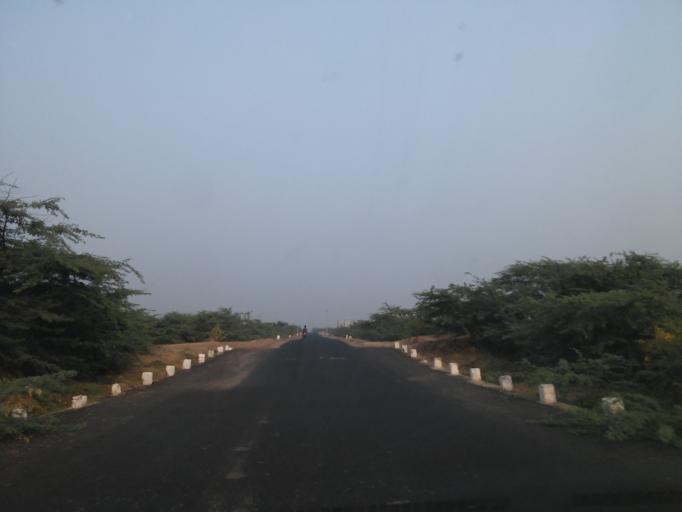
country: IN
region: Gujarat
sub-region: Kachchh
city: Mandvi
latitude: 22.8436
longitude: 69.3124
